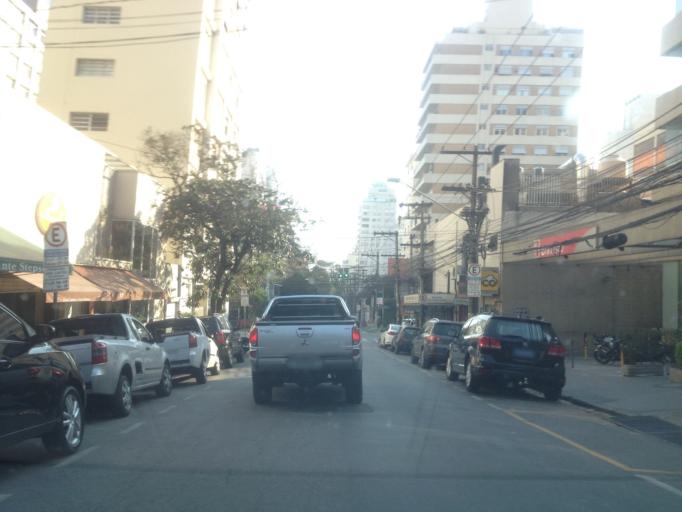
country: BR
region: Sao Paulo
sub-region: Sao Paulo
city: Sao Paulo
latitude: -23.5642
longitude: -46.6647
